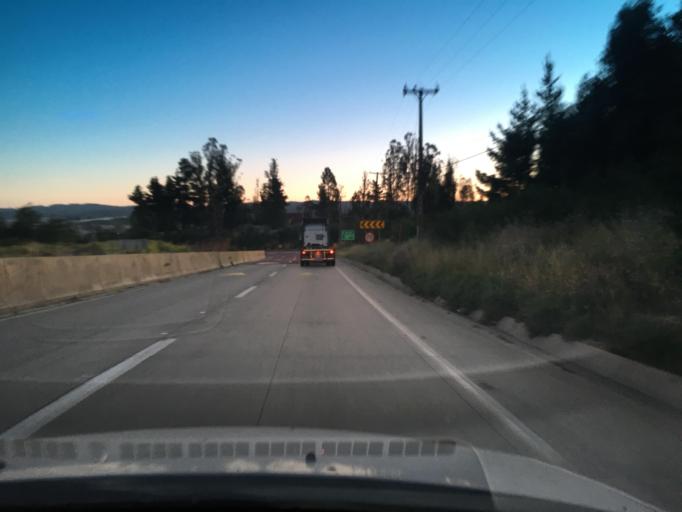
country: CL
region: Valparaiso
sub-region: Provincia de Valparaiso
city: Vina del Mar
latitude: -33.1036
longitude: -71.5728
